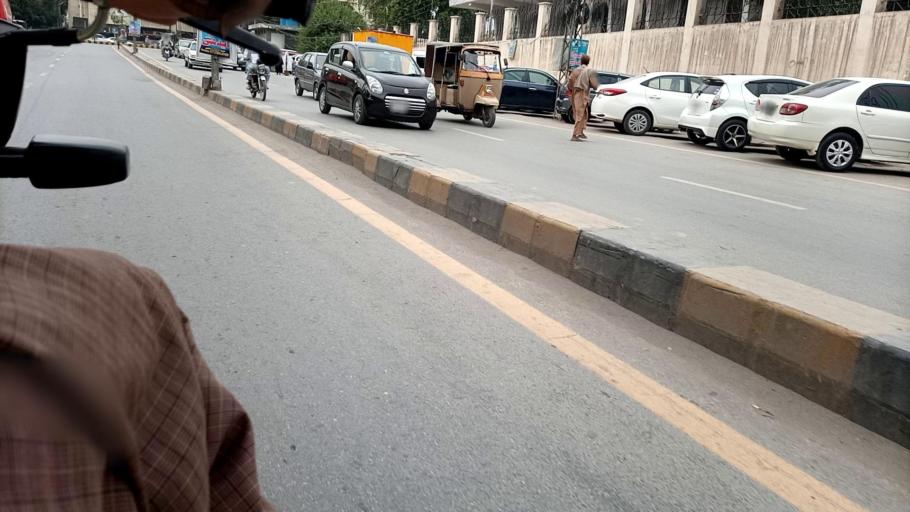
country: PK
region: Khyber Pakhtunkhwa
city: Peshawar
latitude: 33.9986
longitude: 71.5363
